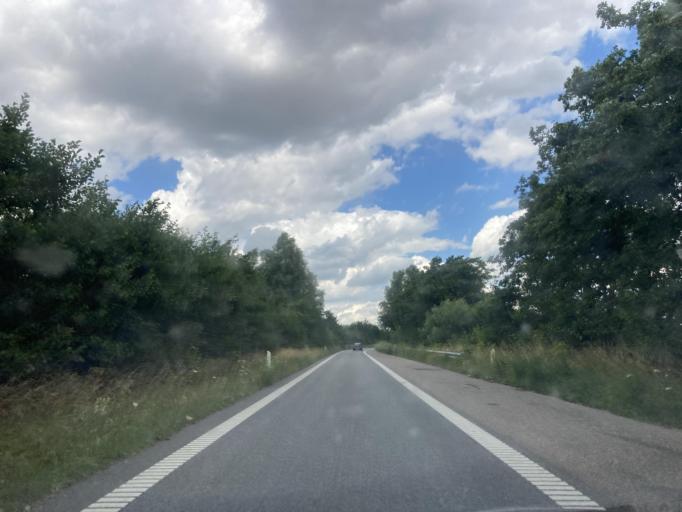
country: DK
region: Zealand
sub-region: Faxe Kommune
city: Haslev
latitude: 55.3414
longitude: 12.0490
